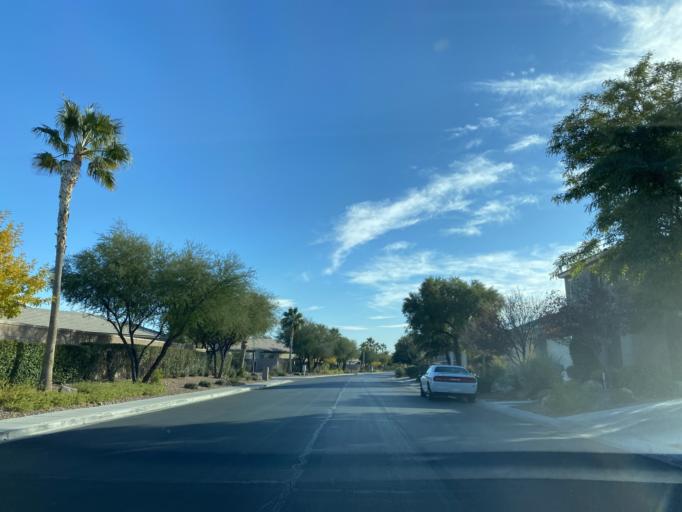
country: US
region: Nevada
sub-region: Clark County
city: North Las Vegas
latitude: 36.3151
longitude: -115.2437
